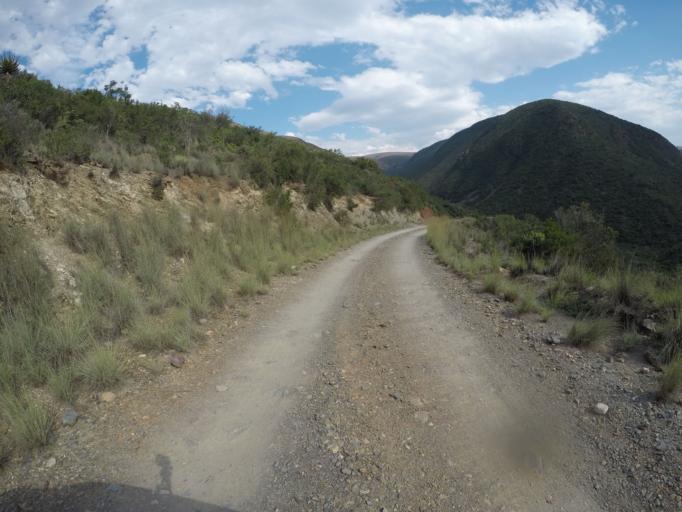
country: ZA
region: Eastern Cape
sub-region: Cacadu District Municipality
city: Kareedouw
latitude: -33.6474
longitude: 24.3392
